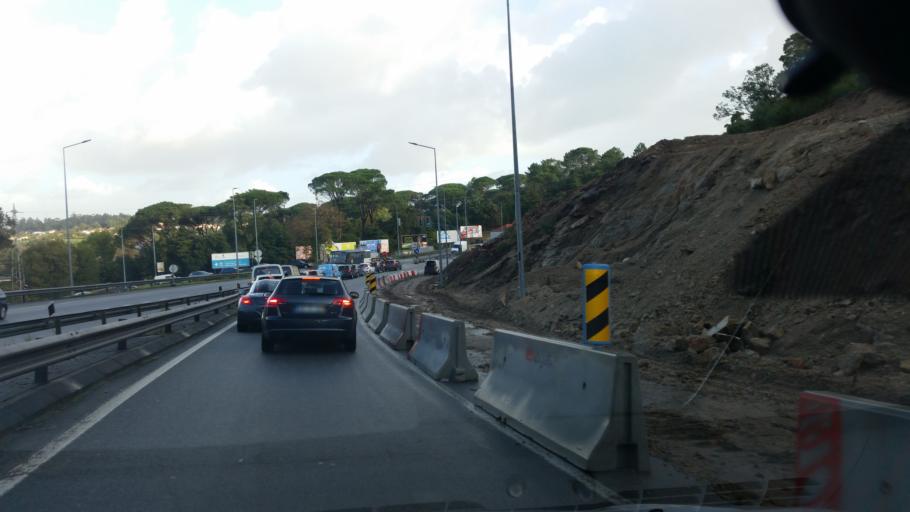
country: PT
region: Porto
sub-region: Santo Tirso
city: Santo Tirso
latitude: 41.3416
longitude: -8.4678
